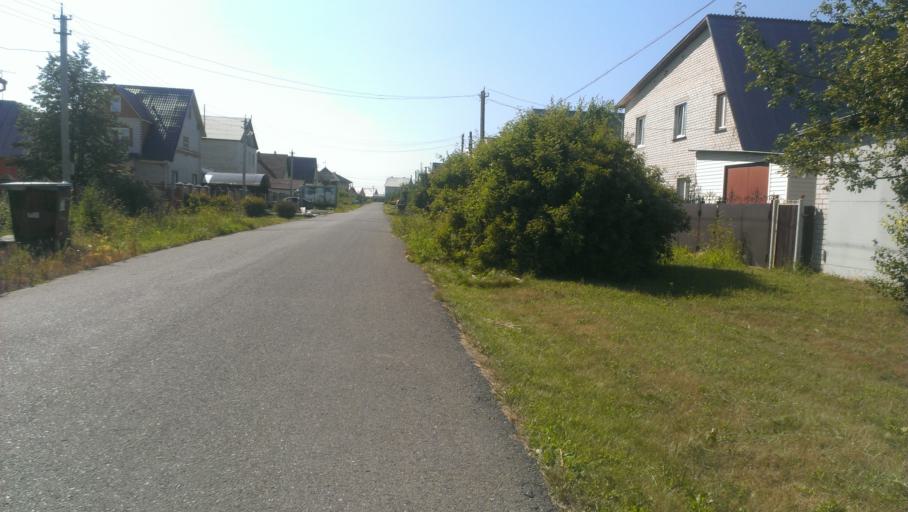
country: RU
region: Altai Krai
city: Novosilikatnyy
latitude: 53.3701
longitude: 83.6568
